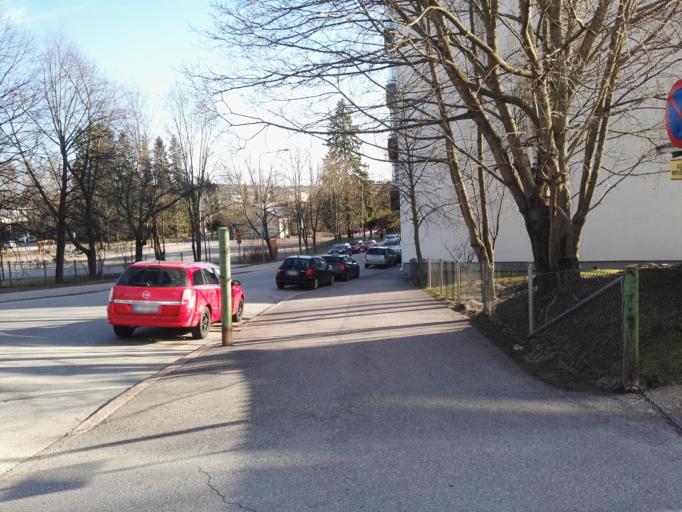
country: FI
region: Paijanne Tavastia
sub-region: Lahti
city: Lahti
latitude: 60.9790
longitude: 25.6657
